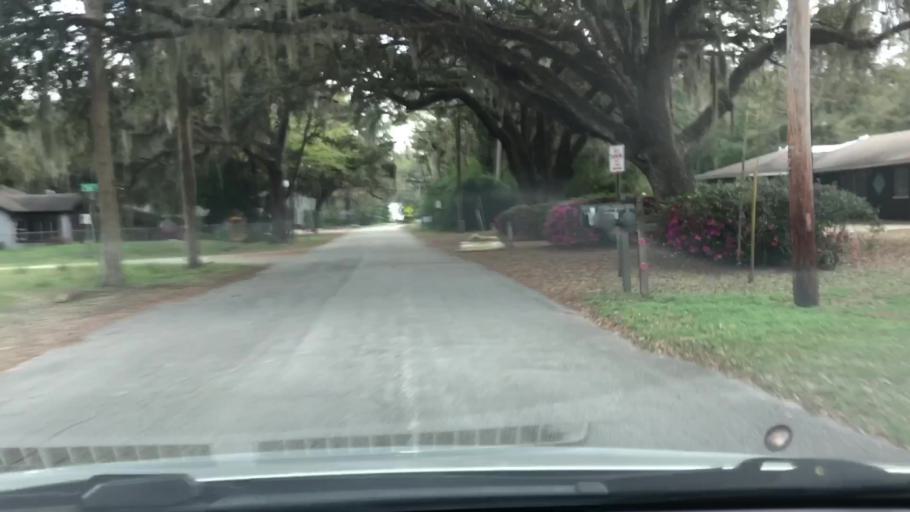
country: US
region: Florida
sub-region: Volusia County
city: Deltona
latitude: 28.8710
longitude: -81.2676
